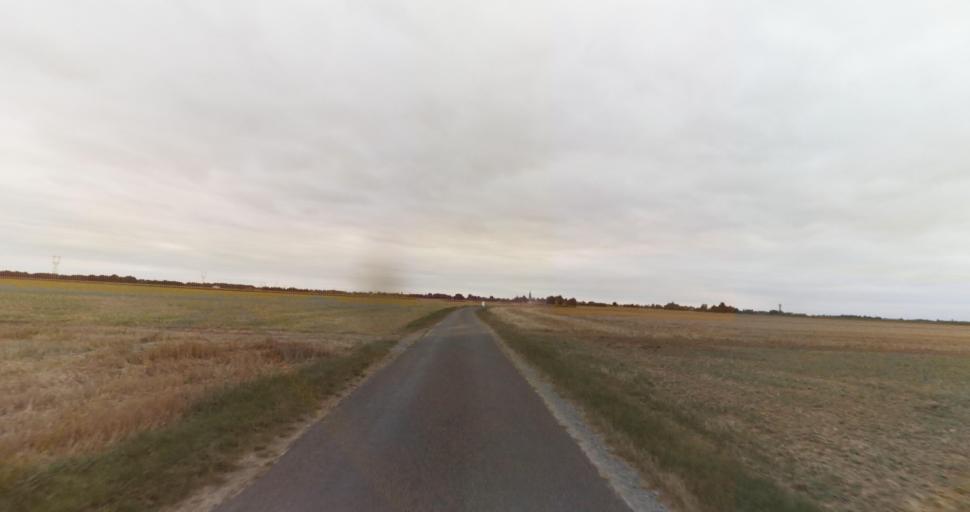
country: FR
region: Haute-Normandie
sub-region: Departement de l'Eure
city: Marcilly-sur-Eure
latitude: 48.8650
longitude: 1.2618
